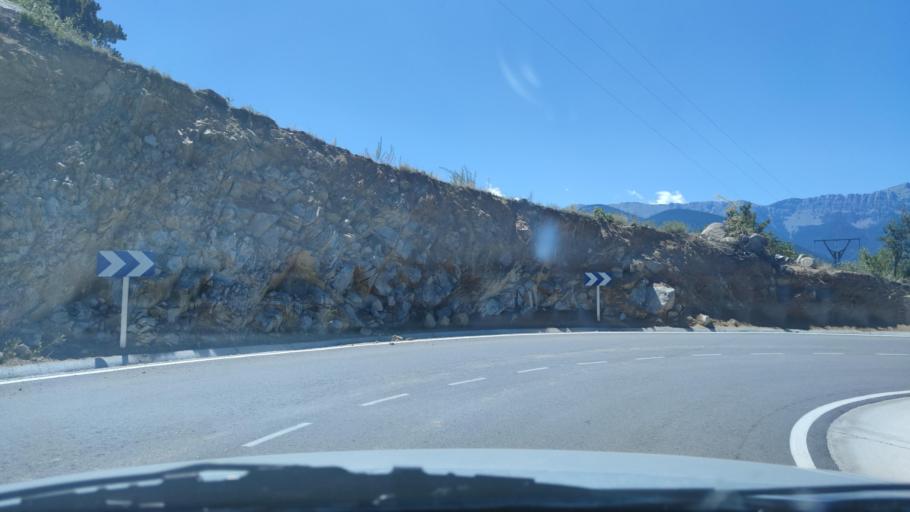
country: ES
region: Catalonia
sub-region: Provincia de Lleida
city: Lles de Cerdanya
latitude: 42.3794
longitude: 1.6908
